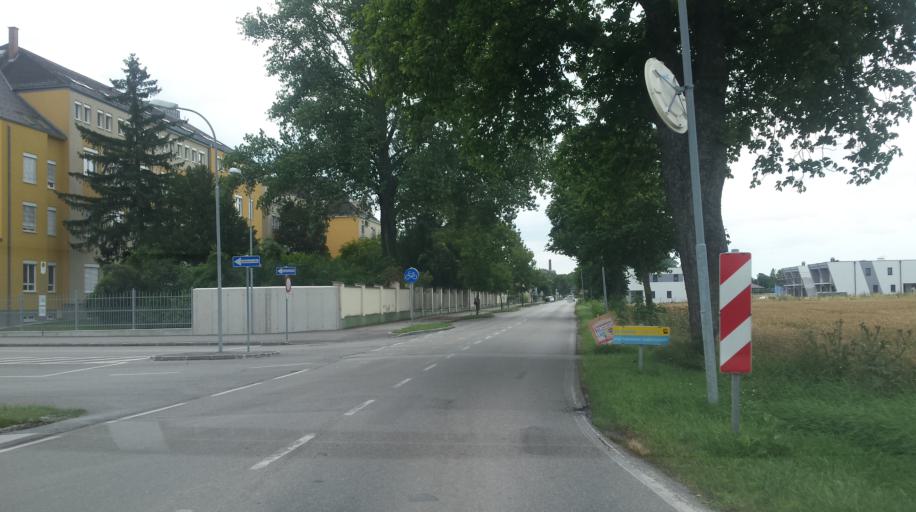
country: AT
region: Lower Austria
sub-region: Politischer Bezirk Baden
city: Ebreichsdorf
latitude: 47.9671
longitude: 16.4306
